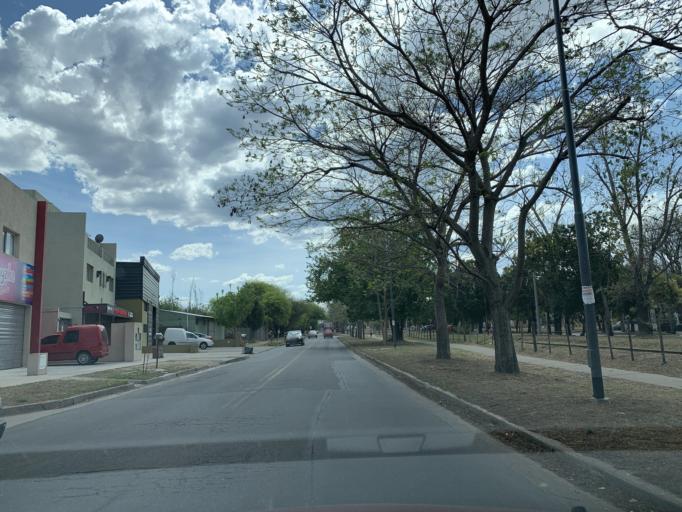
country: AR
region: Cordoba
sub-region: Departamento de Capital
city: Cordoba
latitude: -31.3627
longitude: -64.2226
